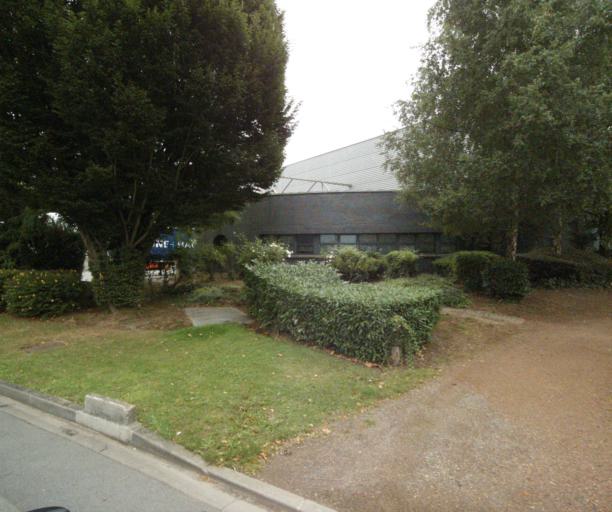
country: FR
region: Nord-Pas-de-Calais
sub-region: Departement du Nord
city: Lezennes
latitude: 50.6157
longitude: 3.1035
